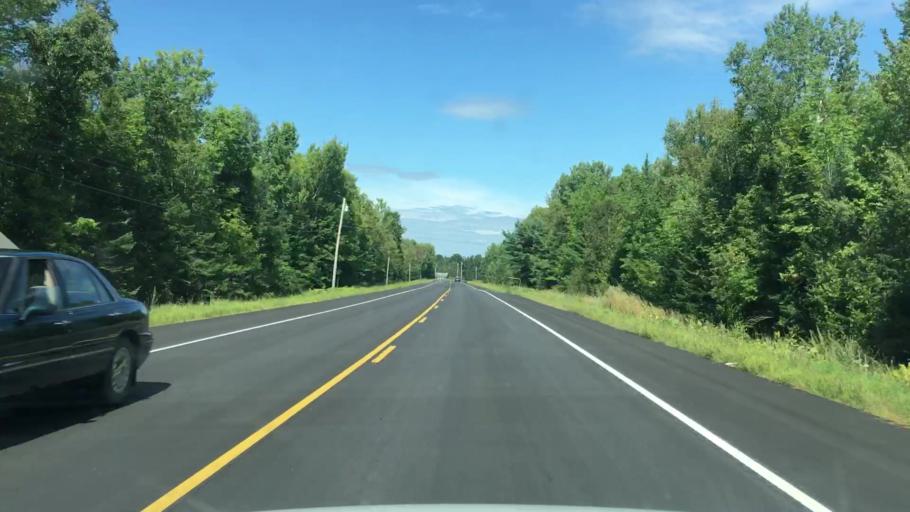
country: US
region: Maine
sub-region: Penobscot County
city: Corinna
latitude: 44.9577
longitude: -69.2646
